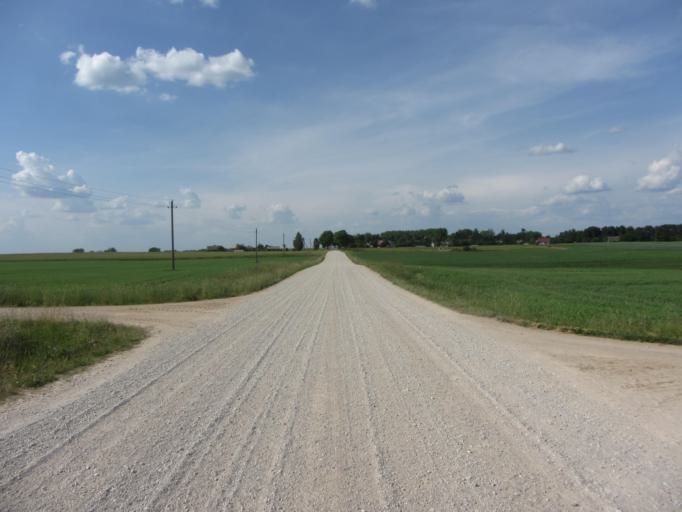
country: LT
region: Kauno apskritis
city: Jonava
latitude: 55.1783
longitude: 24.3760
